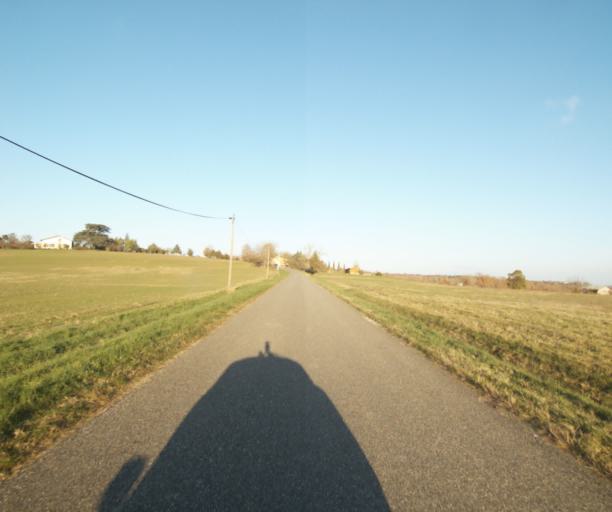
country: FR
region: Midi-Pyrenees
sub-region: Departement du Tarn-et-Garonne
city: Moissac
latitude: 44.1320
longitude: 1.1222
